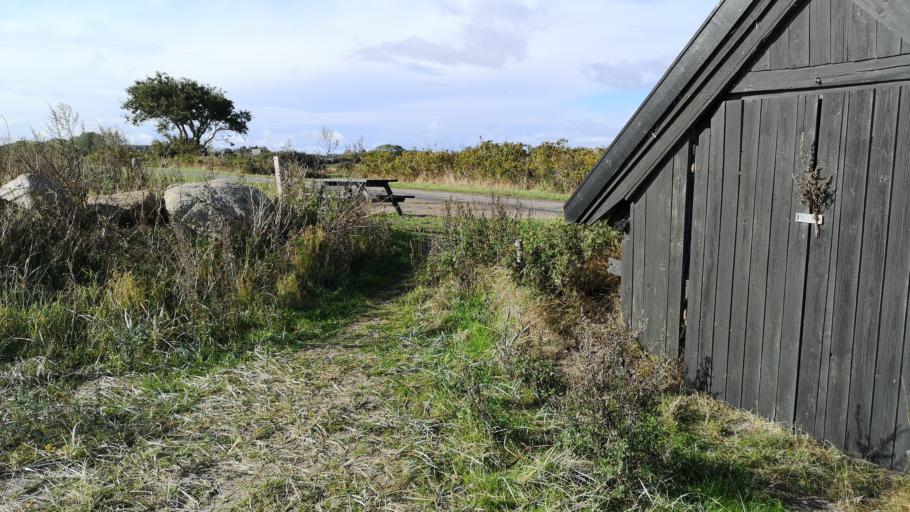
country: DK
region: South Denmark
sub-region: Langeland Kommune
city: Rudkobing
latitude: 54.9456
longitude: 10.8395
